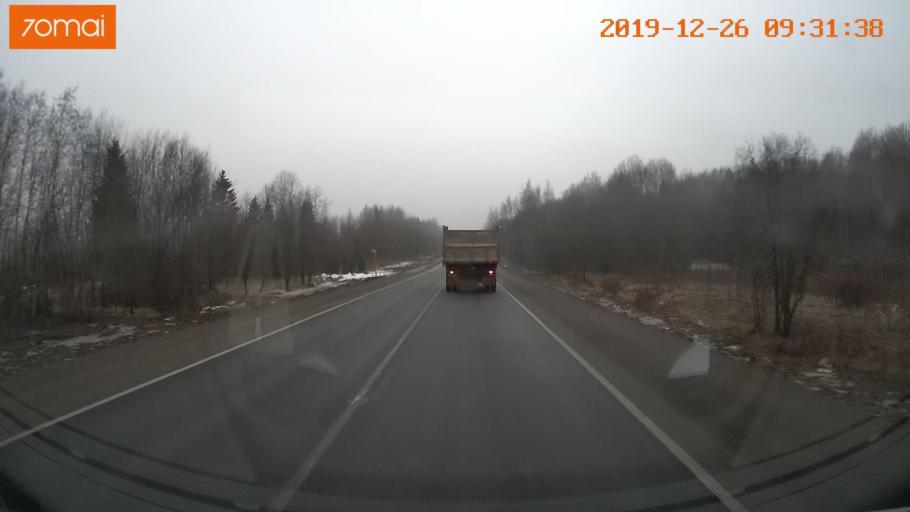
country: RU
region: Vologda
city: Gryazovets
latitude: 59.0707
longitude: 40.1259
